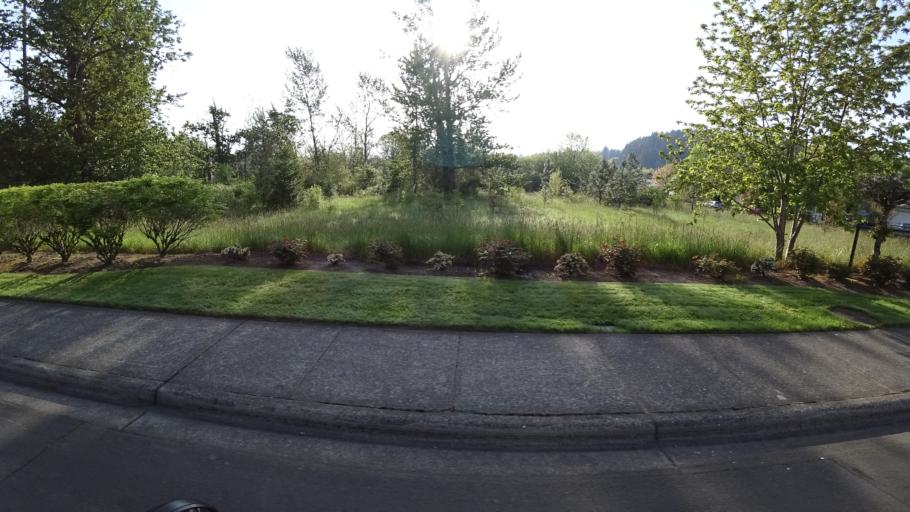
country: US
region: Oregon
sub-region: Washington County
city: King City
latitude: 45.4264
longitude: -122.8410
